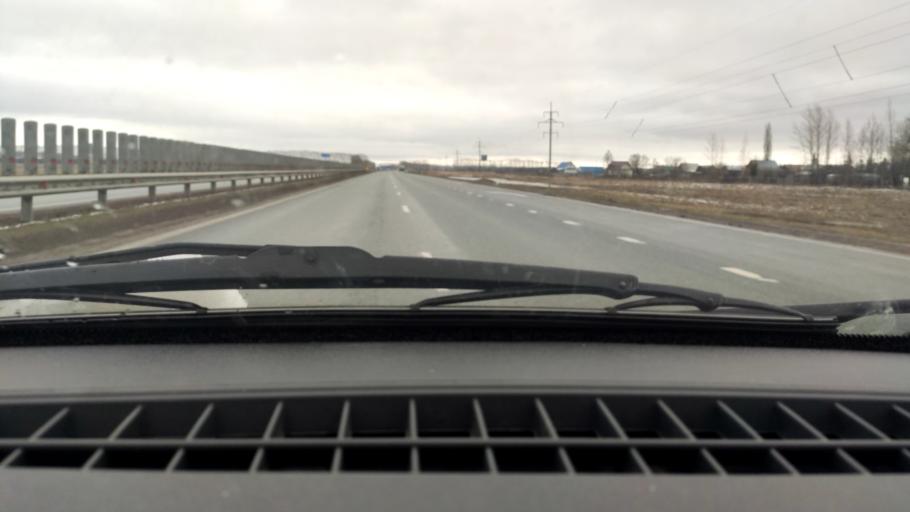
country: RU
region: Bashkortostan
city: Asanovo
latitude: 55.0017
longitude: 55.4951
